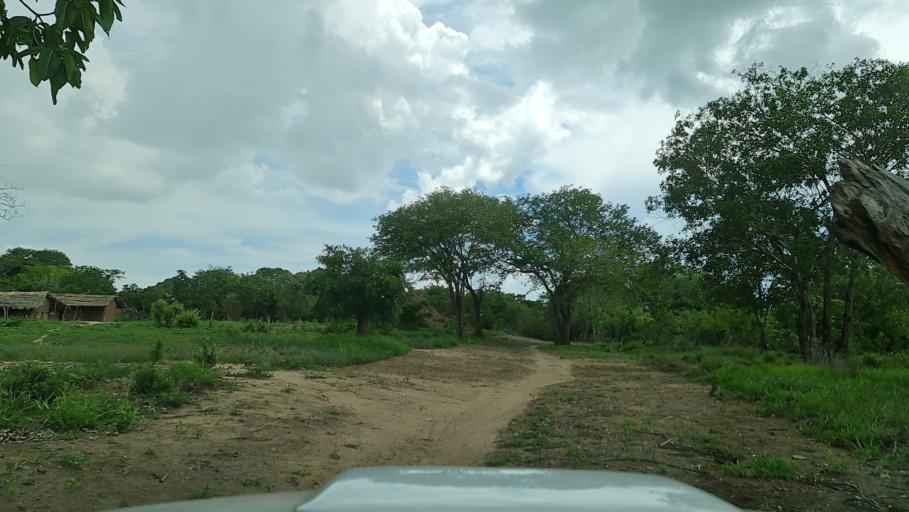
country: MZ
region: Nampula
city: Ilha de Mocambique
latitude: -15.5014
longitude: 40.1583
